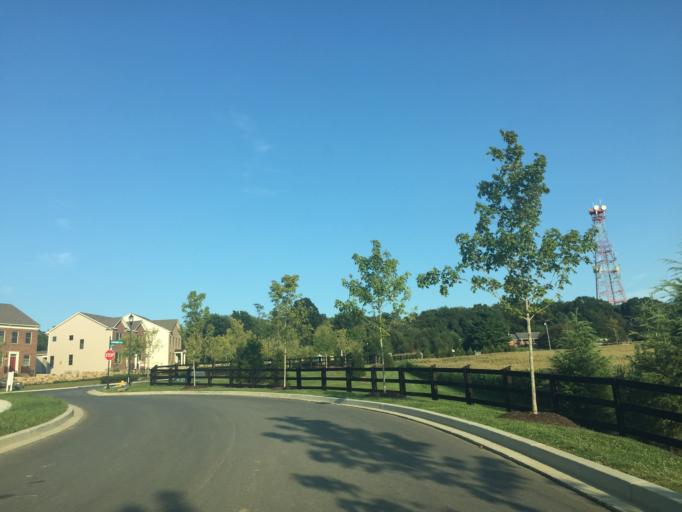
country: US
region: Maryland
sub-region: Frederick County
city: Green Valley
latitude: 39.3516
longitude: -77.2851
